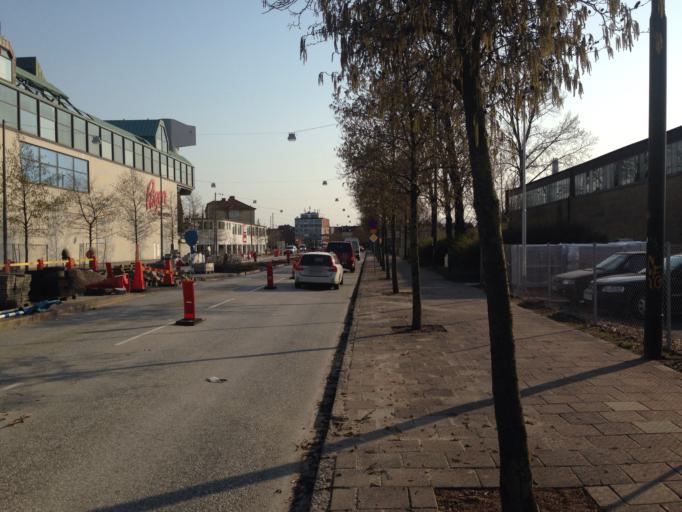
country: SE
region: Skane
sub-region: Malmo
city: Malmoe
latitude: 55.5868
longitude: 13.0191
